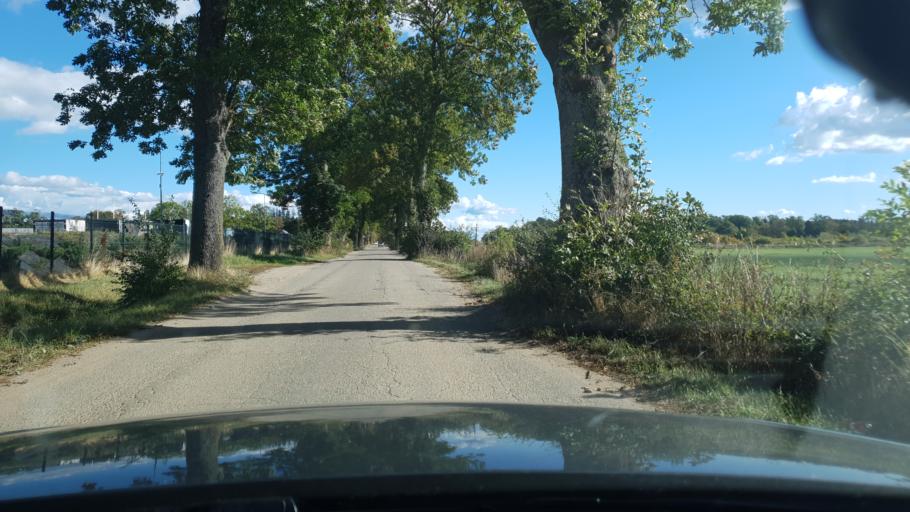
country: PL
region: Pomeranian Voivodeship
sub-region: Powiat pucki
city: Zelistrzewo
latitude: 54.6866
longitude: 18.4533
